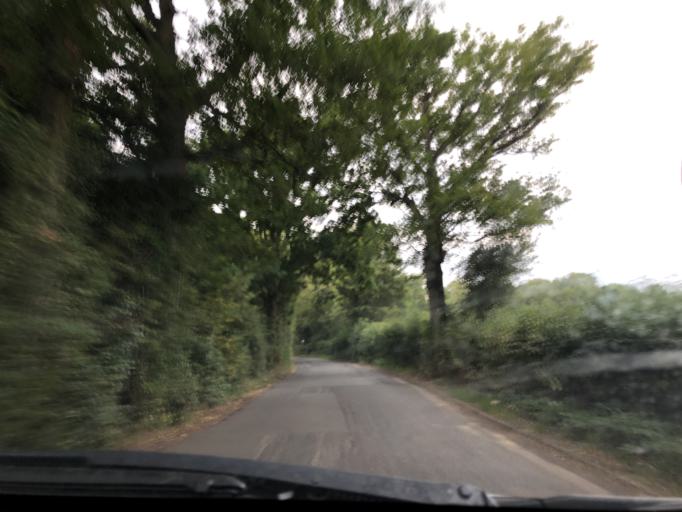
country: GB
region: England
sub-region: Kent
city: Sevenoaks
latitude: 51.2375
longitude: 0.2378
